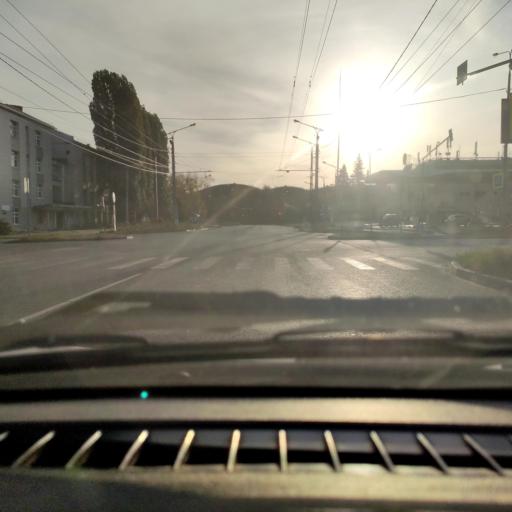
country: RU
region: Samara
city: Tol'yatti
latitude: 53.5205
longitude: 49.4293
